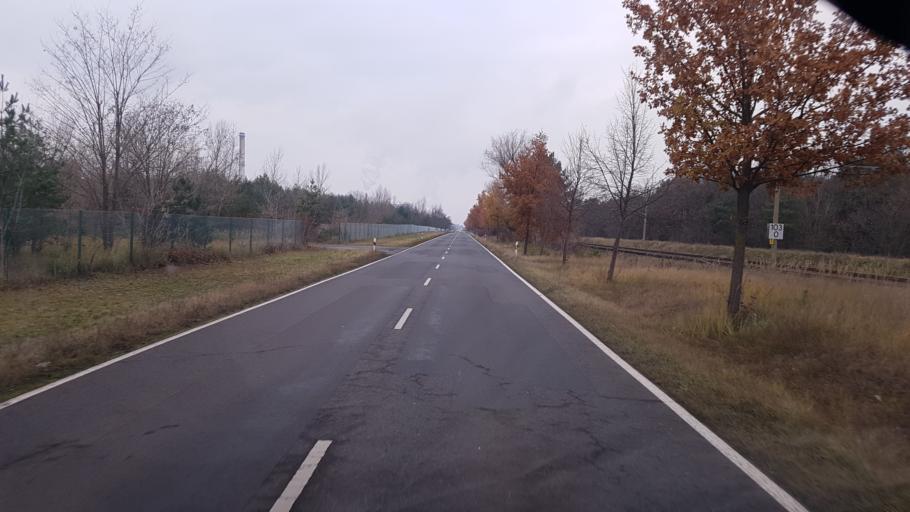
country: DE
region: Brandenburg
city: Eisenhuettenstadt
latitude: 52.1615
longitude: 14.6543
